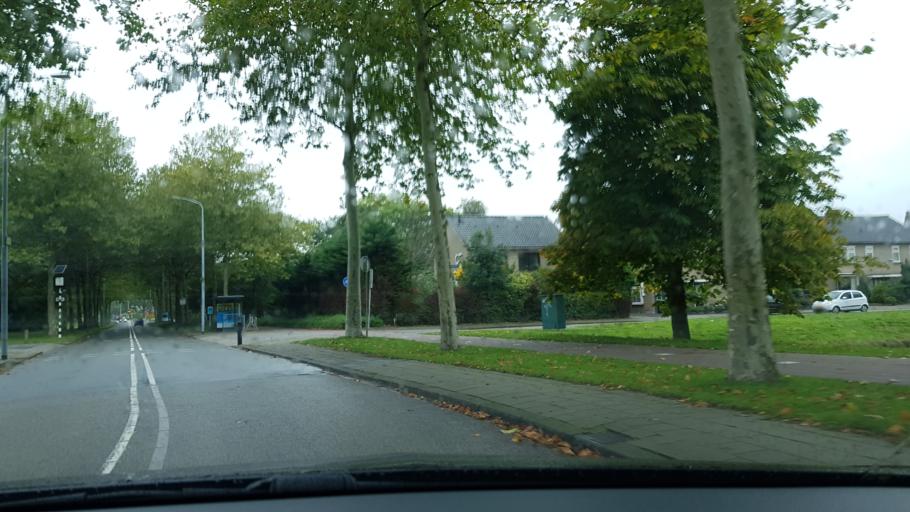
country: NL
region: North Holland
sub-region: Gemeente Haarlemmermeer
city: Hoofddorp
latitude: 52.3113
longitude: 4.6875
